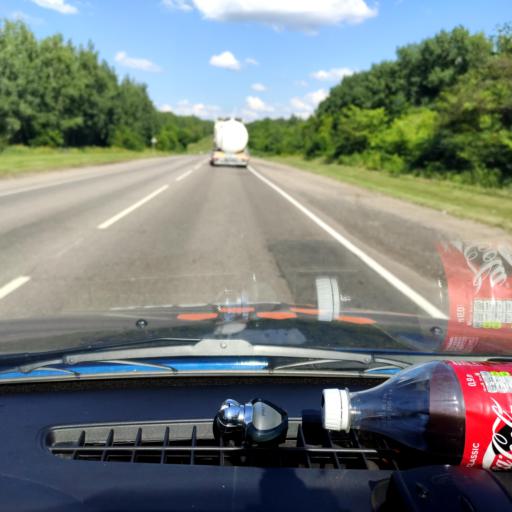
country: RU
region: Lipetsk
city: Kazaki
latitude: 52.6357
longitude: 38.2872
